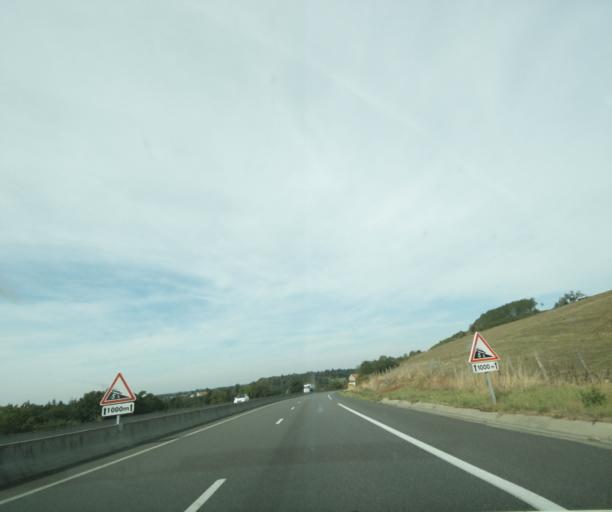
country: FR
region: Auvergne
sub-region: Departement de l'Allier
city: Lapalisse
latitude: 46.2244
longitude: 3.6555
